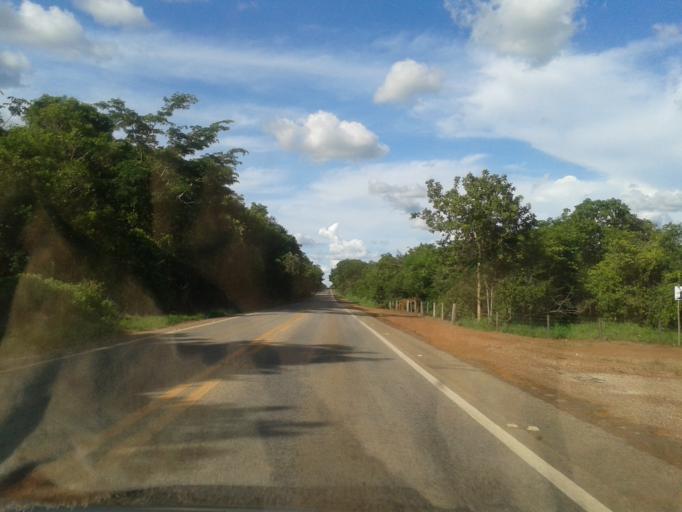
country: BR
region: Goias
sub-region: Mozarlandia
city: Mozarlandia
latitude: -14.6952
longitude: -50.5447
